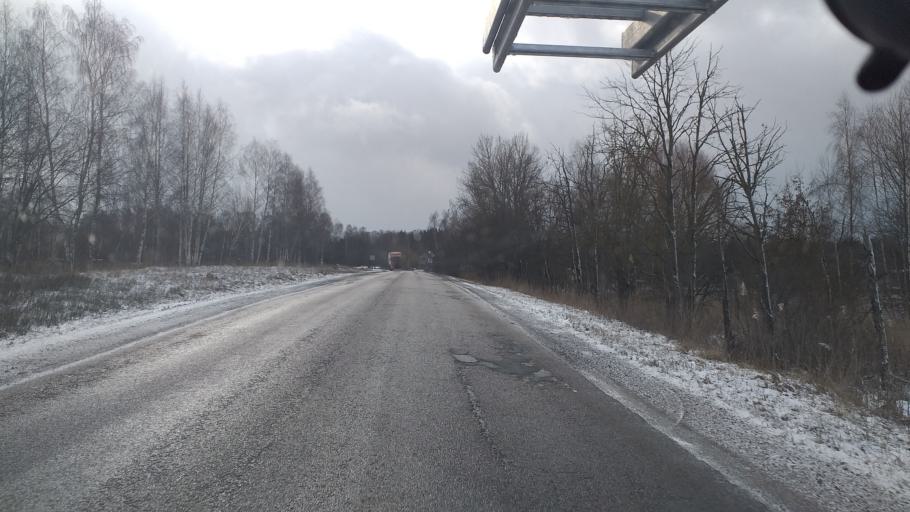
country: LV
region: Riga
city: Bolderaja
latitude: 56.9895
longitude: 24.0316
